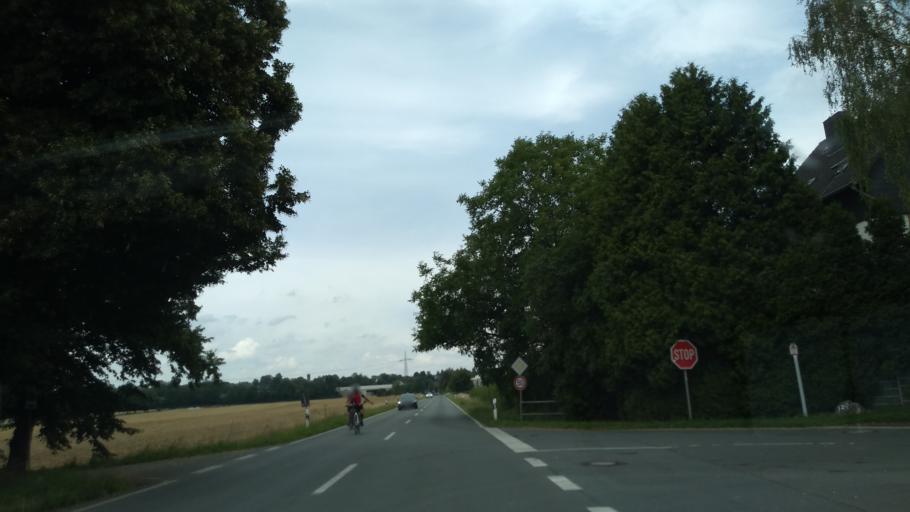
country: DE
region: North Rhine-Westphalia
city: Schwerte
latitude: 51.4664
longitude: 7.6046
